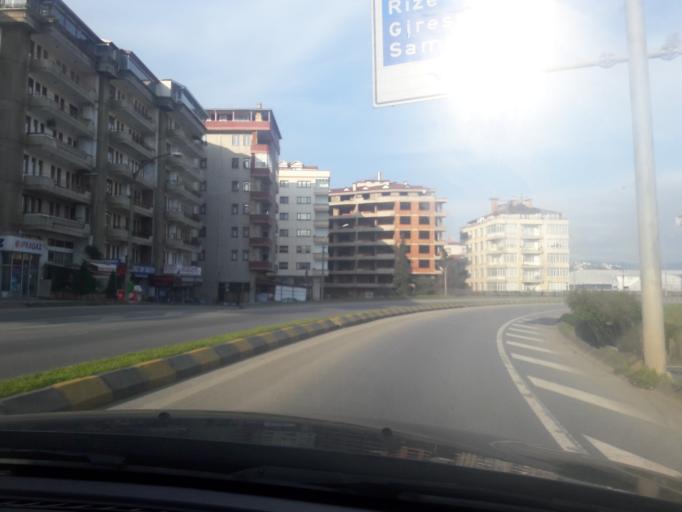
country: TR
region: Trabzon
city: Trabzon
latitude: 40.9961
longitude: 39.6760
